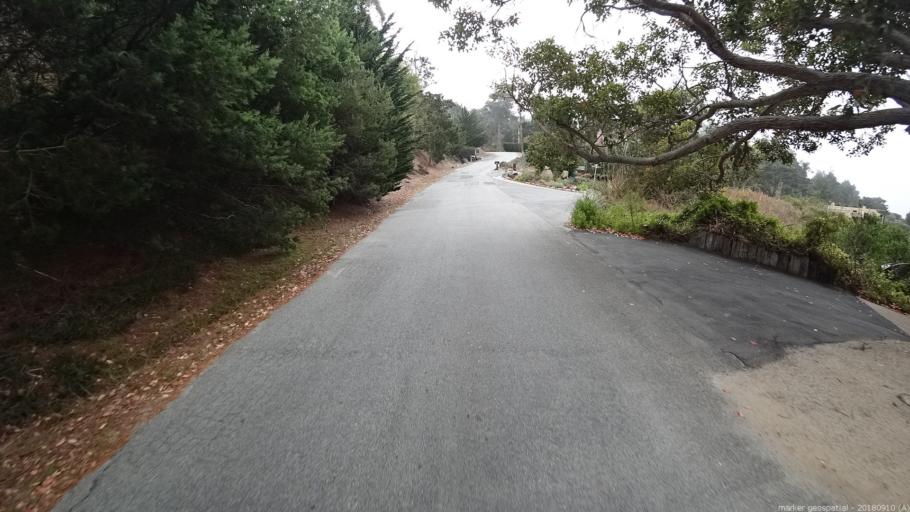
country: US
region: California
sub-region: Monterey County
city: Carmel-by-the-Sea
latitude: 36.4880
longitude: -121.9362
